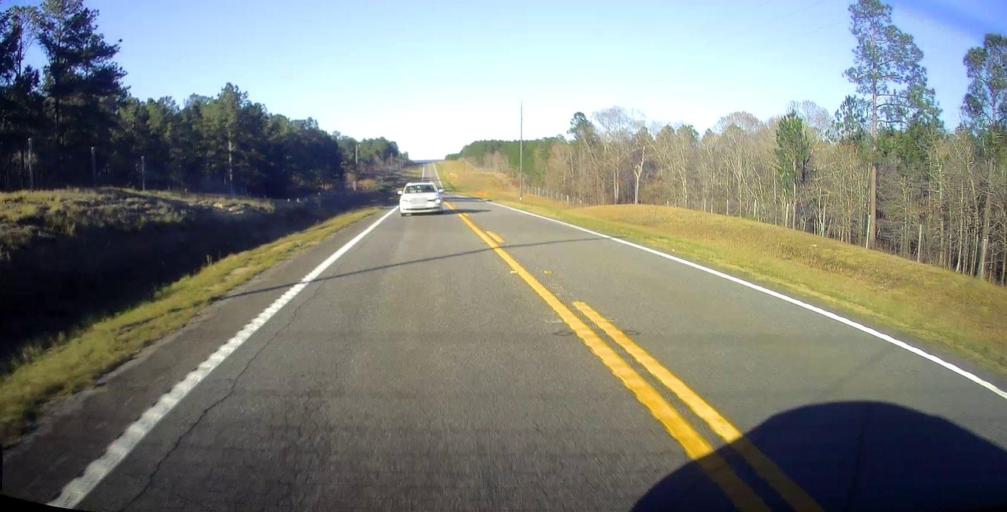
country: US
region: Georgia
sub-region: Taylor County
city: Butler
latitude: 32.4869
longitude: -84.3476
